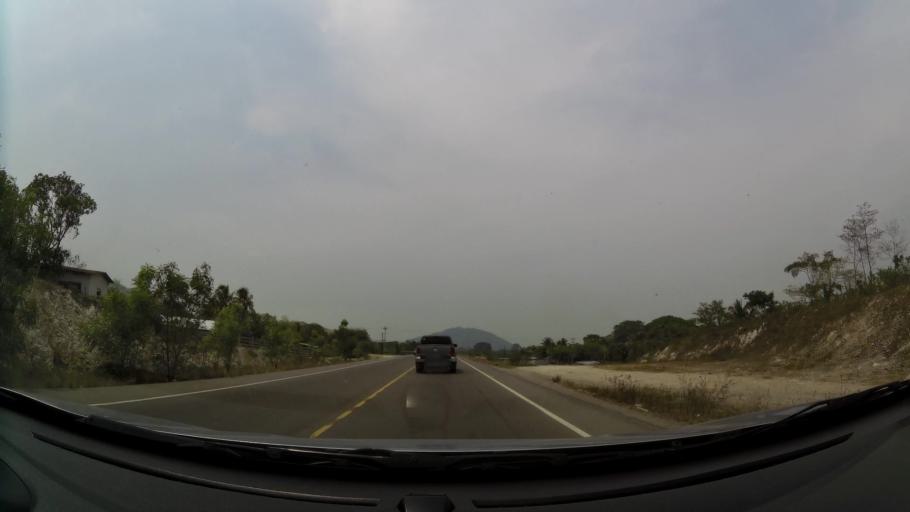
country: HN
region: Cortes
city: Potrerillos
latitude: 15.2364
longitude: -87.9580
